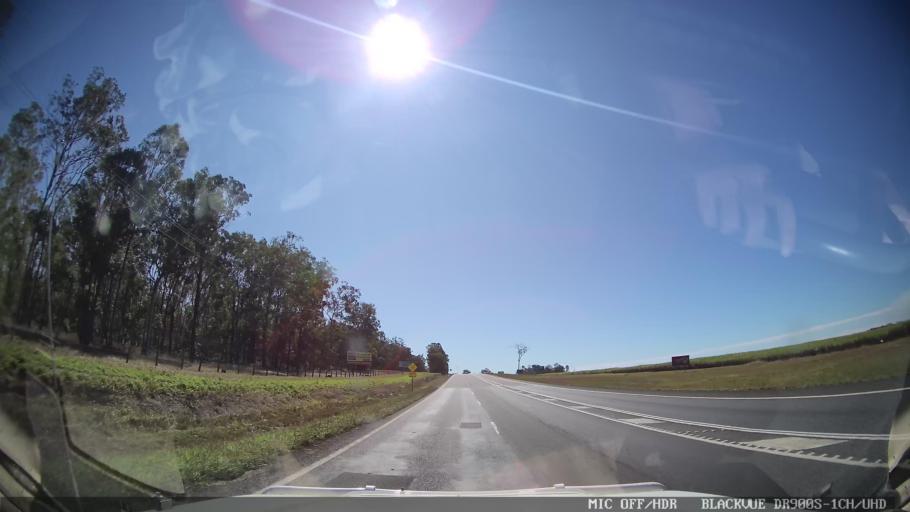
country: AU
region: Queensland
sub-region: Fraser Coast
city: Maryborough
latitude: -25.6439
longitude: 152.6380
